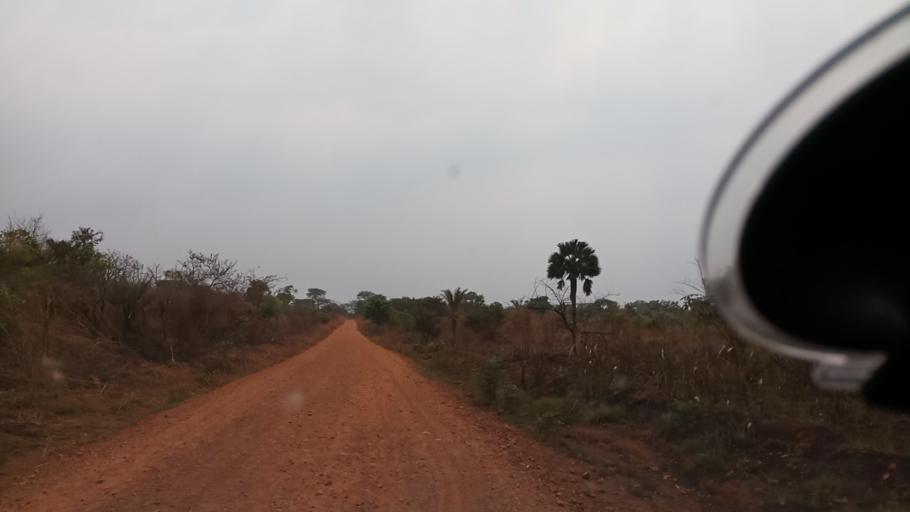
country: ZM
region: Luapula
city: Nchelenge
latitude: -9.0962
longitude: 28.3224
